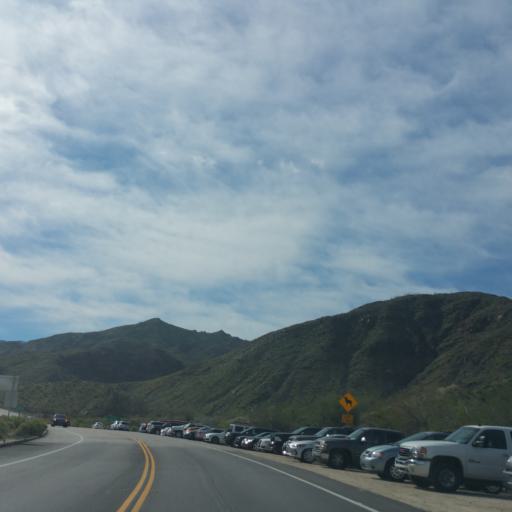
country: US
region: California
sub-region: Riverside County
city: Palm Desert
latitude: 33.6709
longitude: -116.4093
